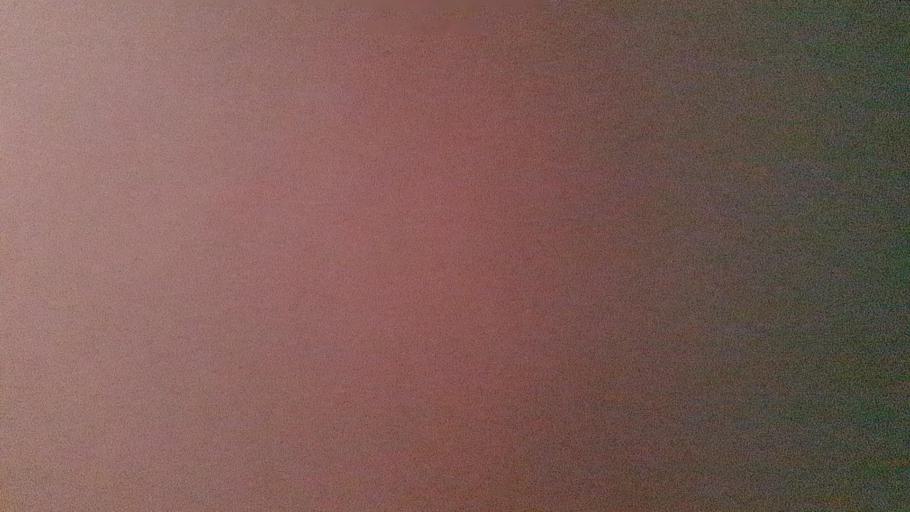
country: FI
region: Lapland
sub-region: Torniolaakso
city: Ylitornio
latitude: 66.2374
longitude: 23.6784
